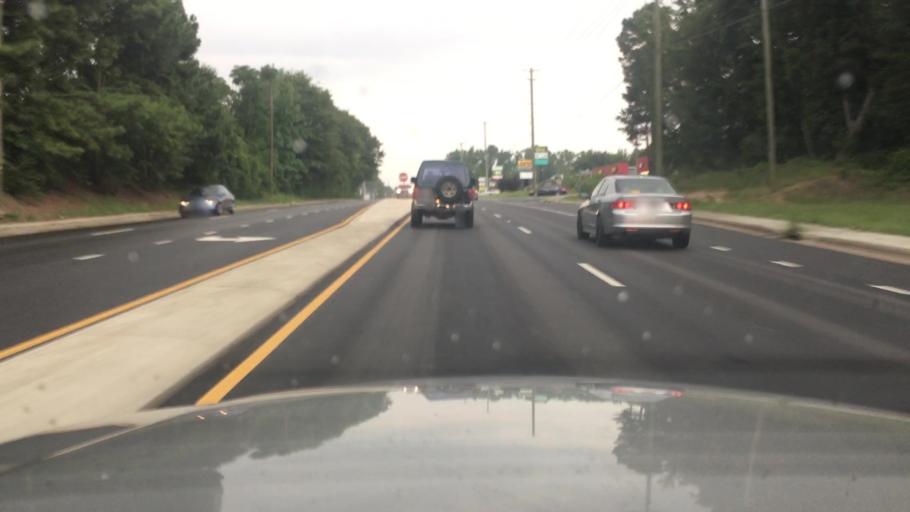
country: US
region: North Carolina
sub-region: Cumberland County
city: Fort Bragg
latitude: 35.0710
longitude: -79.0124
